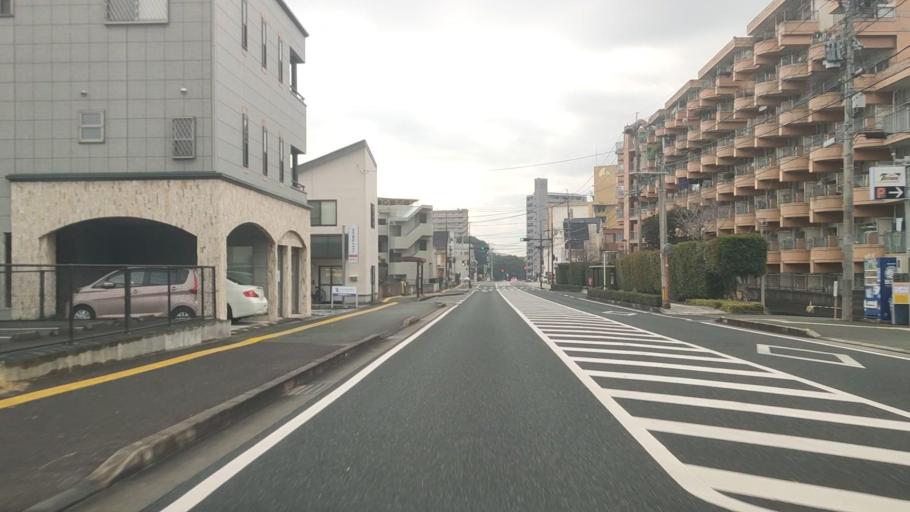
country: JP
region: Kumamoto
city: Kumamoto
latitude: 32.7903
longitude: 130.7396
